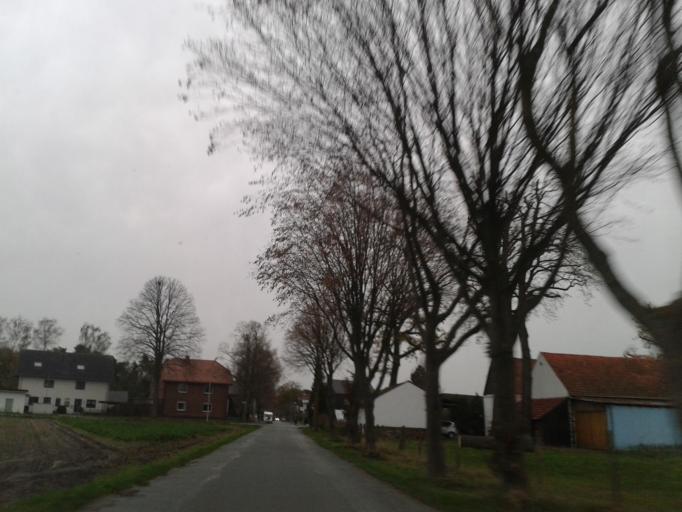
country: DE
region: North Rhine-Westphalia
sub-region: Regierungsbezirk Detmold
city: Paderborn
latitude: 51.7589
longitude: 8.7415
